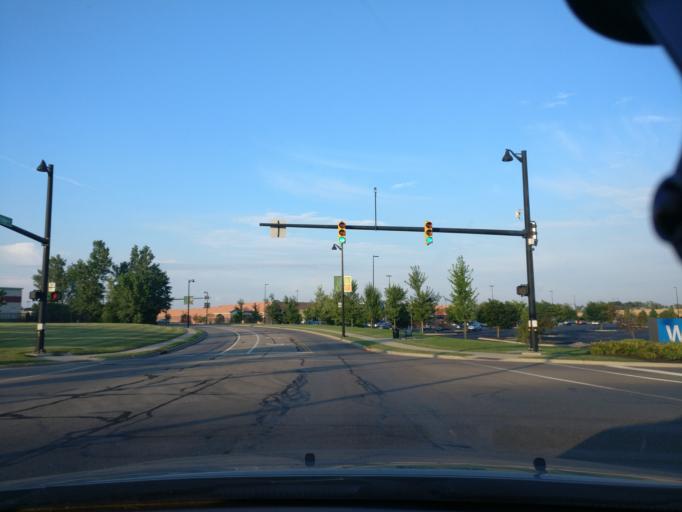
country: US
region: Ohio
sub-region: Montgomery County
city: Centerville
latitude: 39.6299
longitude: -84.2149
